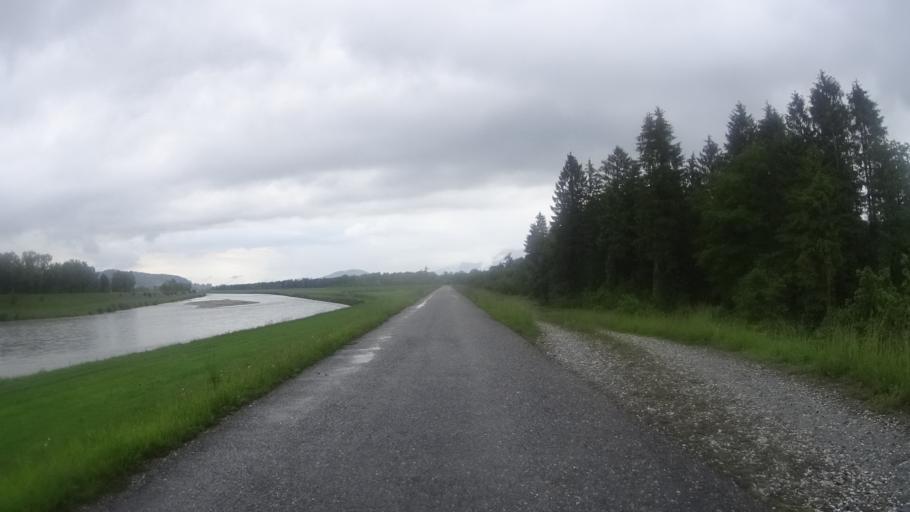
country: CH
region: Saint Gallen
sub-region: Wahlkreis Rheintal
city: Ruthi
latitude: 47.2777
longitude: 9.5445
